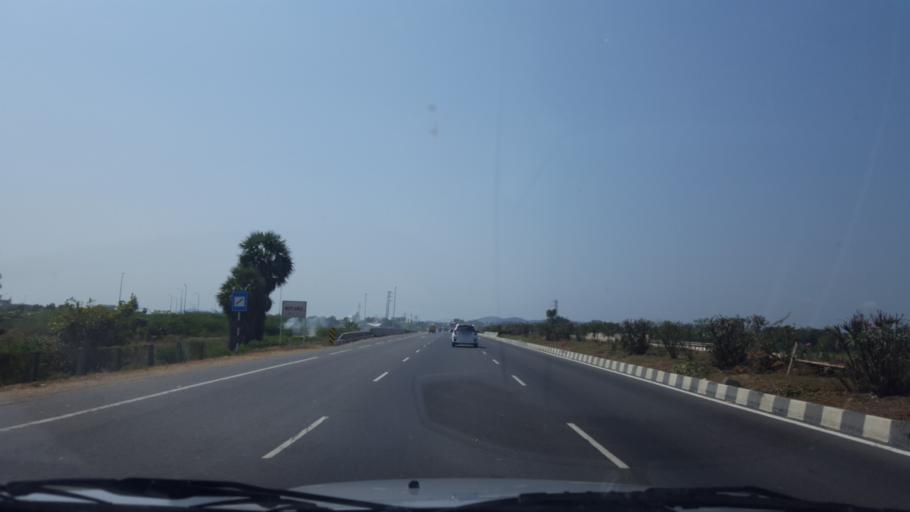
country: IN
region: Andhra Pradesh
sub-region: Guntur
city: Chilakalurupet
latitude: 16.0097
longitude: 80.1166
